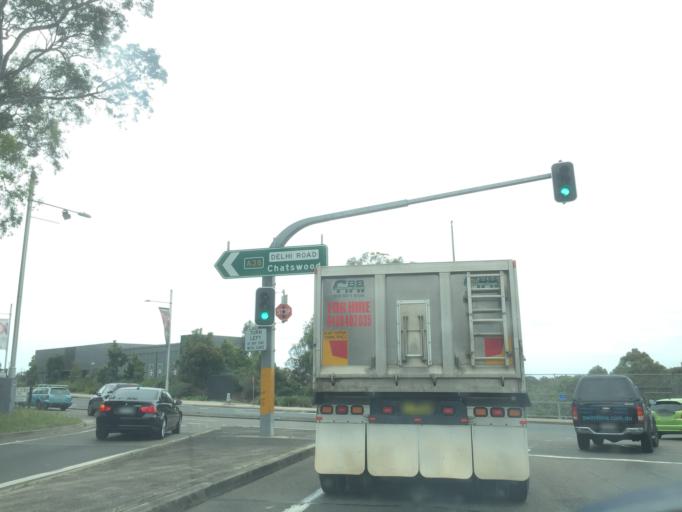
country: AU
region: New South Wales
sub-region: Ryde
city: North Ryde
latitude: -33.7937
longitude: 151.1362
